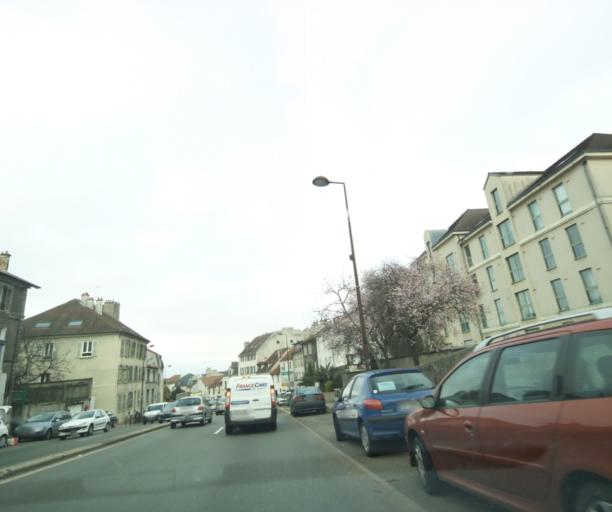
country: FR
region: Ile-de-France
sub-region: Departement des Yvelines
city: Le Port-Marly
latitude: 48.8780
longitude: 2.1075
